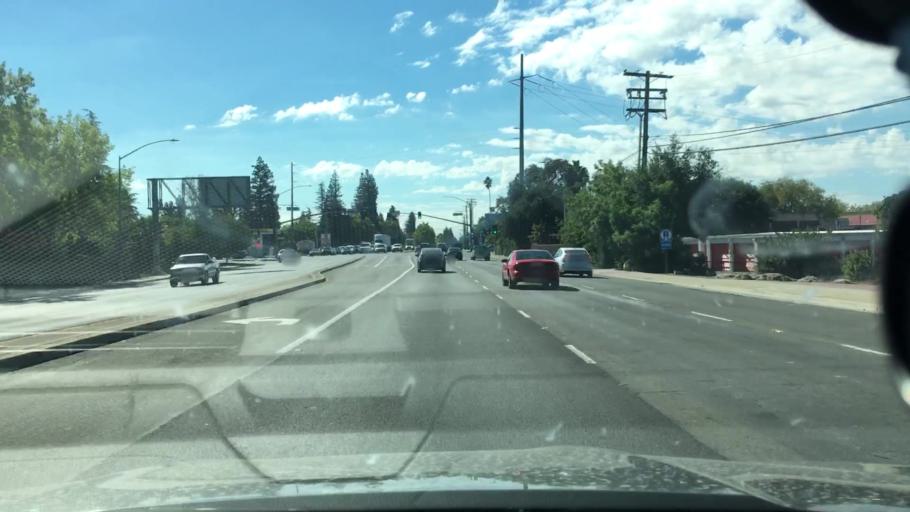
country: US
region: California
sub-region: Sacramento County
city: Arden-Arcade
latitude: 38.6385
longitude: -121.3834
